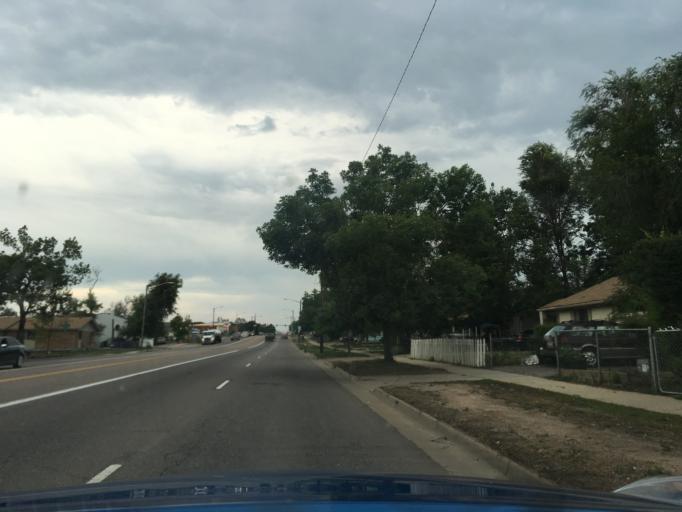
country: US
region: Colorado
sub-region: Arapahoe County
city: Sheridan
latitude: 39.6710
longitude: -105.0252
